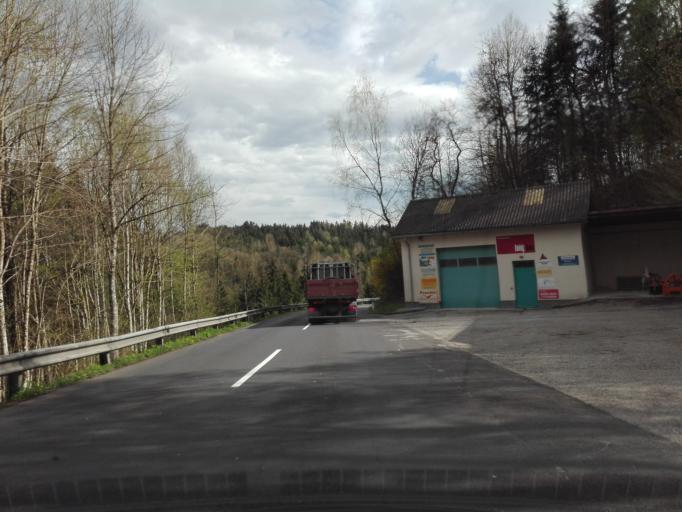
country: AT
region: Upper Austria
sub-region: Politischer Bezirk Rohrbach
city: Kleinzell im Muehlkreis
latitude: 48.4863
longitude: 14.0047
